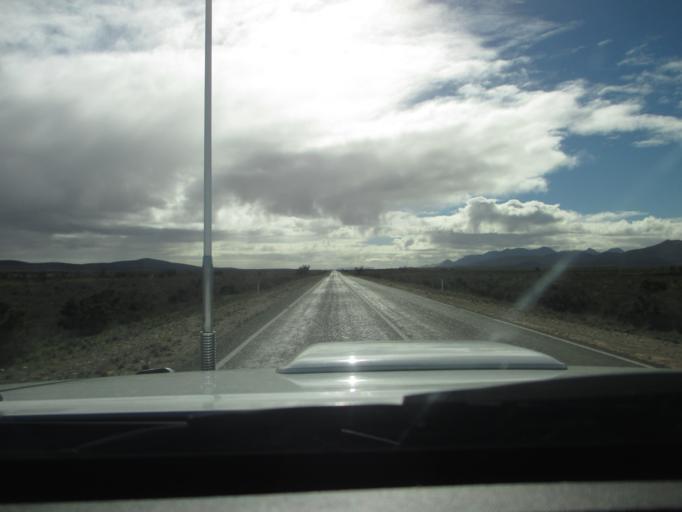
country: AU
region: South Australia
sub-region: Flinders Ranges
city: Quorn
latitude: -31.6722
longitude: 138.3699
